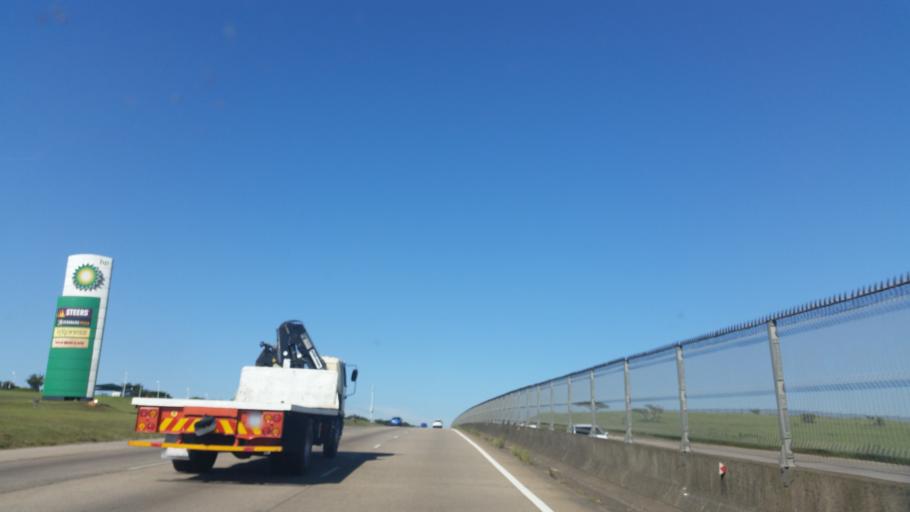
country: ZA
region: KwaZulu-Natal
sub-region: eThekwini Metropolitan Municipality
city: Mpumalanga
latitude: -29.7408
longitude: 30.6347
